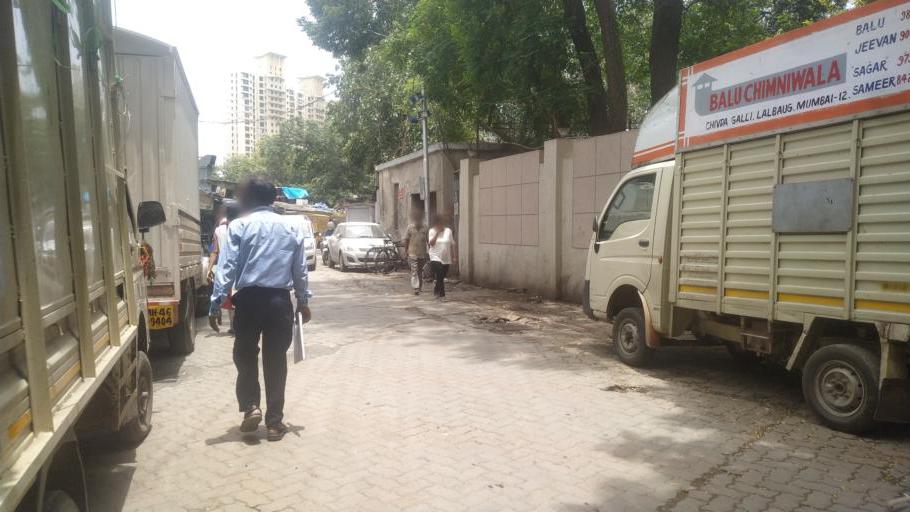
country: IN
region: Maharashtra
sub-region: Mumbai Suburban
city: Mumbai
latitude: 18.9914
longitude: 72.8371
